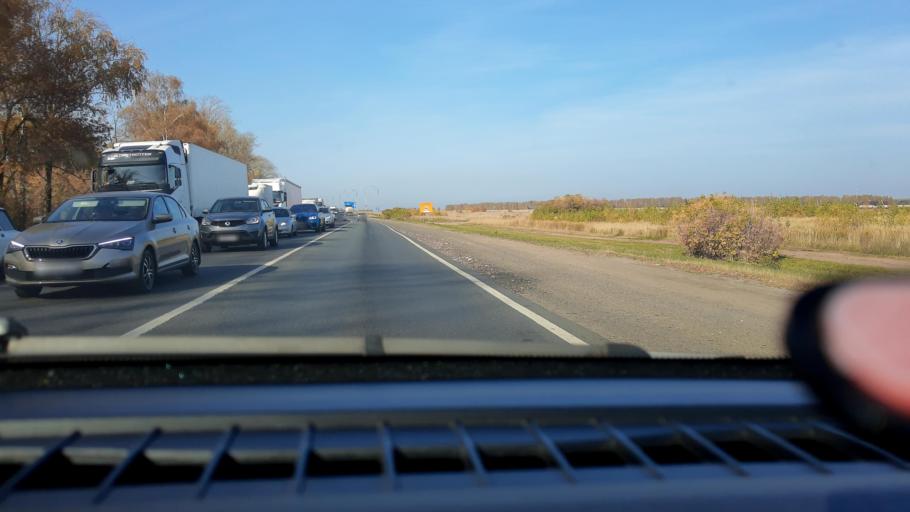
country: RU
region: Nizjnij Novgorod
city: Kstovo
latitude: 56.1218
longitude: 44.2712
